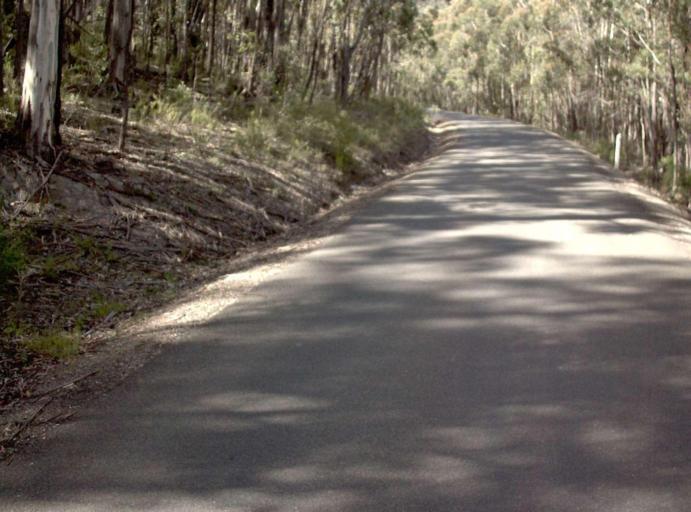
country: AU
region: Victoria
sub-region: East Gippsland
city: Lakes Entrance
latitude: -37.4403
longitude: 148.1318
